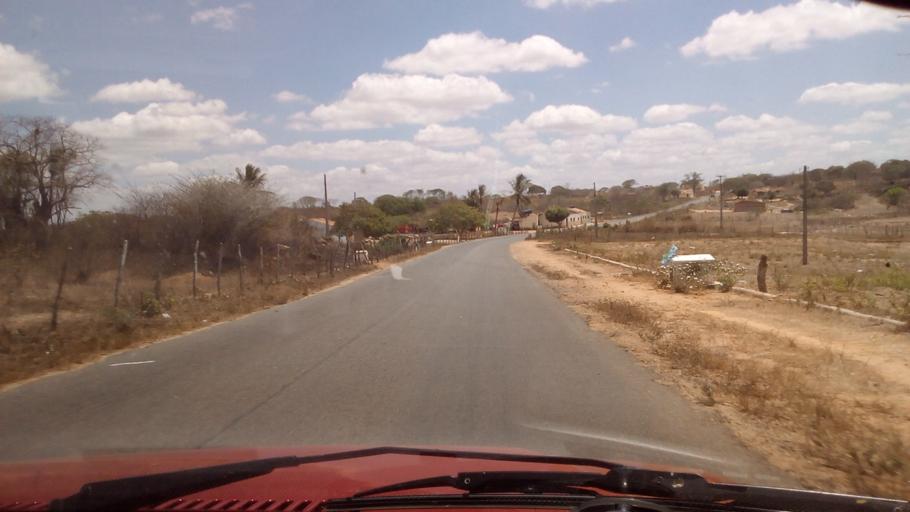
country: BR
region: Paraiba
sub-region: Cacimba De Dentro
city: Cacimba de Dentro
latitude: -6.6131
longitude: -35.8059
